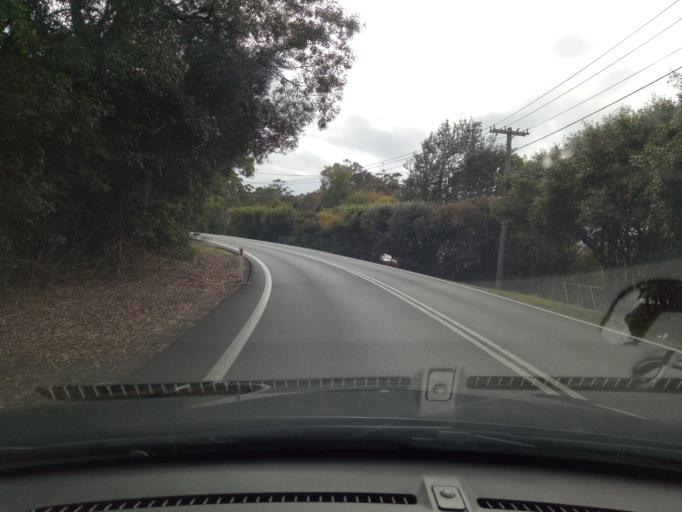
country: AU
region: New South Wales
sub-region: Gosford Shire
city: Holgate
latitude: -33.3975
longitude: 151.4006
